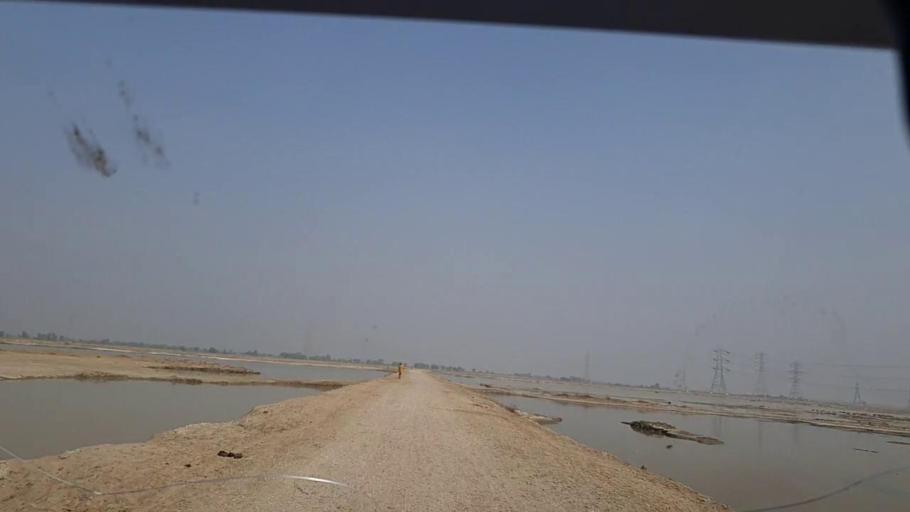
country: PK
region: Sindh
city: Shikarpur
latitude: 28.0299
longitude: 68.6254
